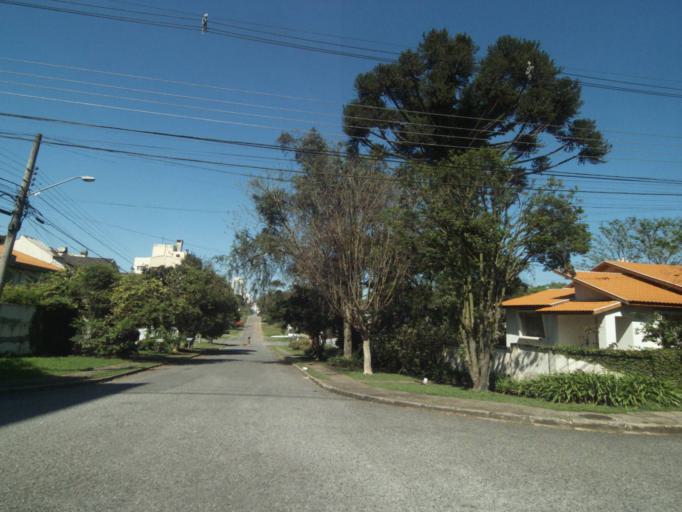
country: BR
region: Parana
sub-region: Curitiba
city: Curitiba
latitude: -25.4007
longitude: -49.2501
